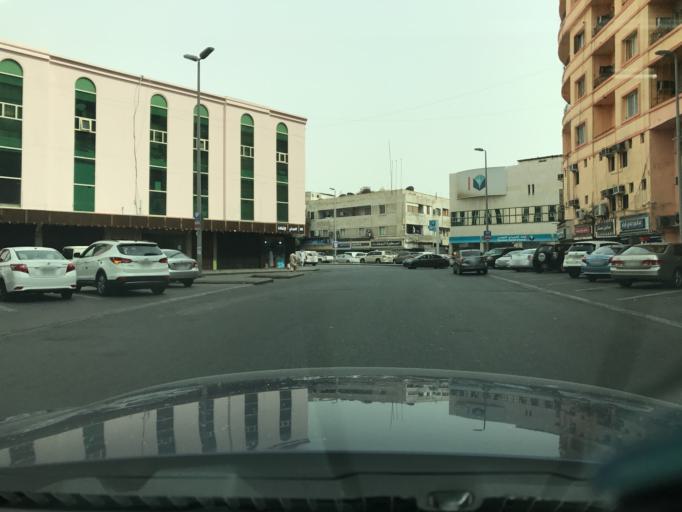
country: SA
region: Makkah
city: Jeddah
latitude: 21.4814
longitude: 39.1835
